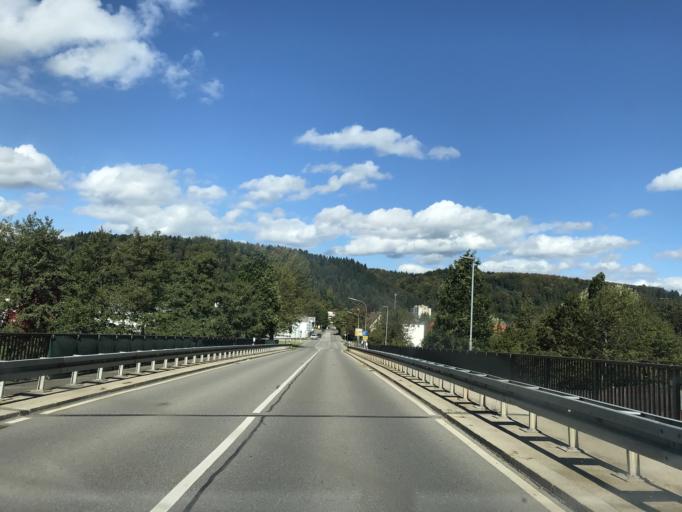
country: DE
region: Baden-Wuerttemberg
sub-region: Freiburg Region
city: Schopfheim
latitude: 47.6421
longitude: 7.8170
